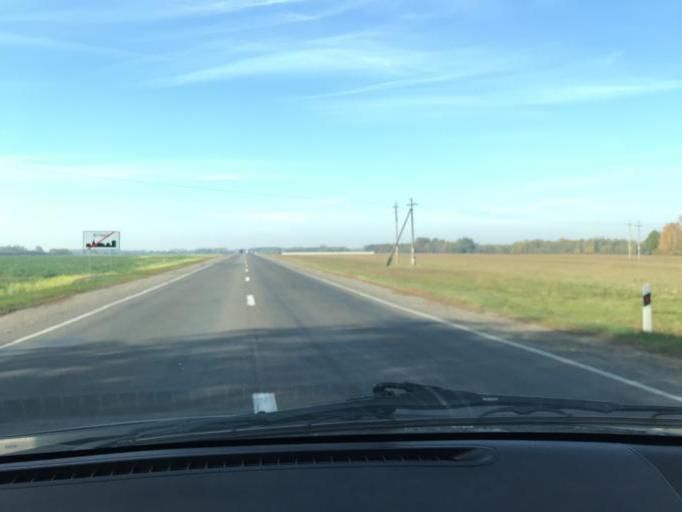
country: BY
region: Brest
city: Luninyets
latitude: 52.2744
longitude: 26.9208
